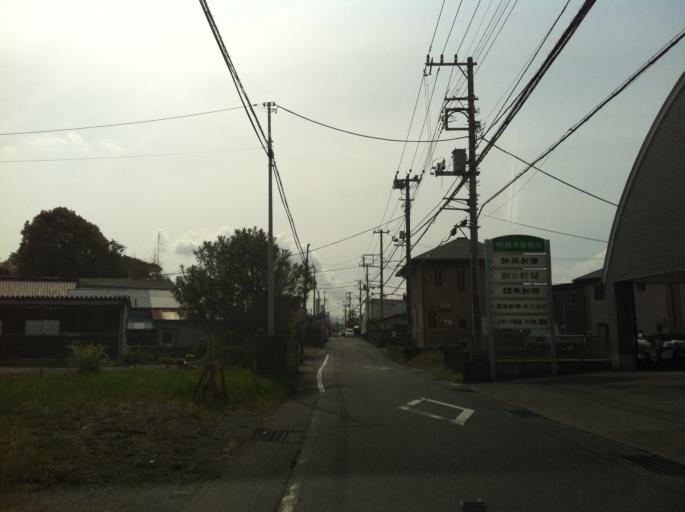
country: JP
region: Shizuoka
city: Numazu
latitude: 35.1322
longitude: 138.8182
